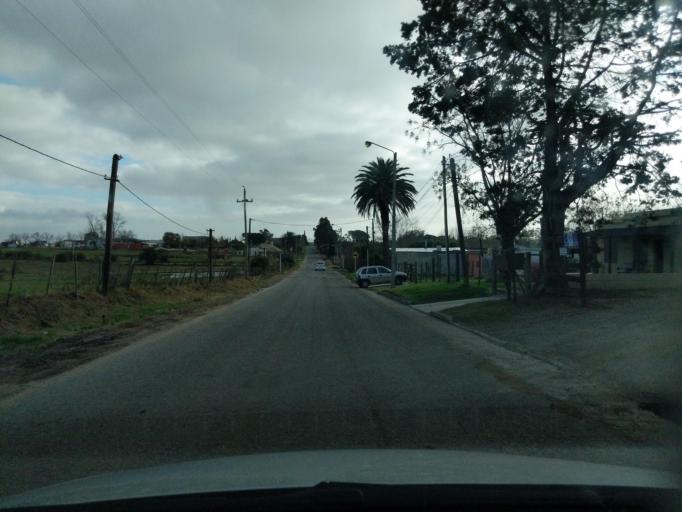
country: UY
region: Florida
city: Florida
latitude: -34.0814
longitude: -56.2120
